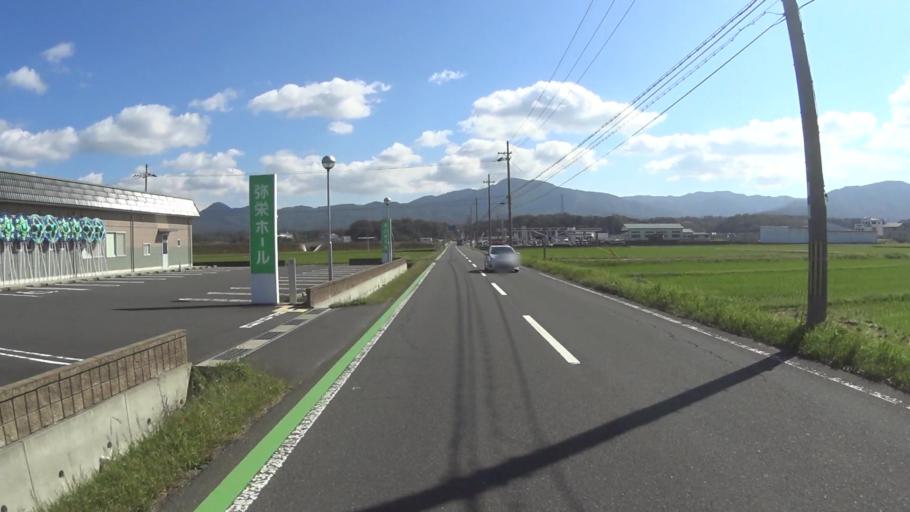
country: JP
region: Kyoto
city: Miyazu
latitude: 35.6703
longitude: 135.0839
